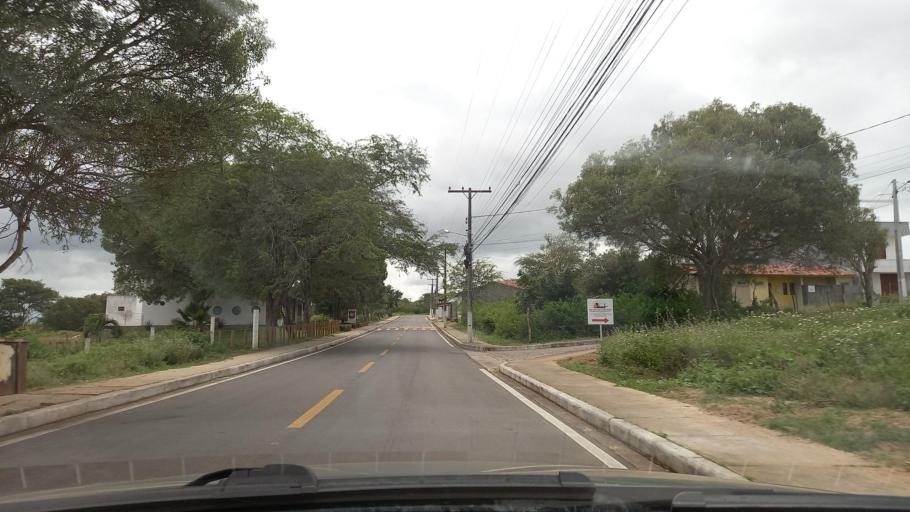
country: BR
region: Sergipe
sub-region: Caninde De Sao Francisco
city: Caninde de Sao Francisco
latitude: -9.6201
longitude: -37.7661
